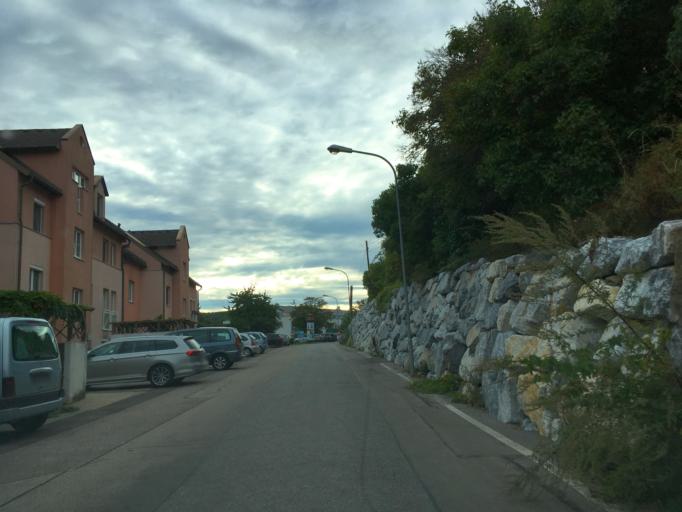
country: AT
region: Lower Austria
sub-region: Politischer Bezirk Tulln
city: Wordern
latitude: 48.3117
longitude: 16.2532
